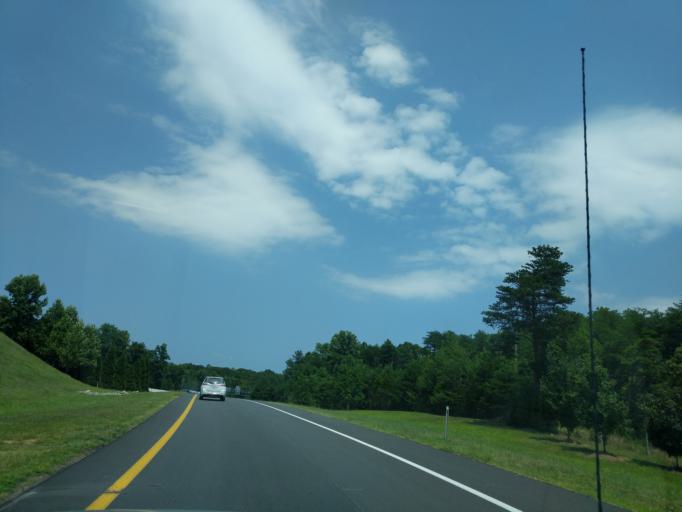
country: US
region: South Carolina
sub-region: Greenville County
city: Greer
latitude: 34.8756
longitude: -82.2134
